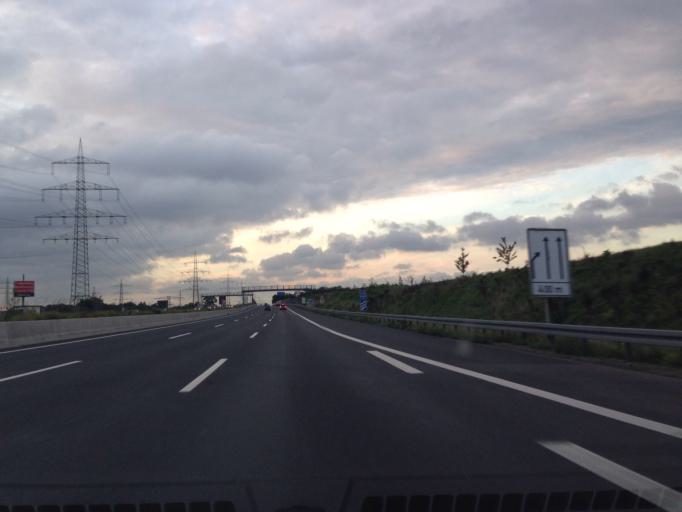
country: DE
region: North Rhine-Westphalia
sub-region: Regierungsbezirk Dusseldorf
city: Kaarst
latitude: 51.2121
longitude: 6.6465
